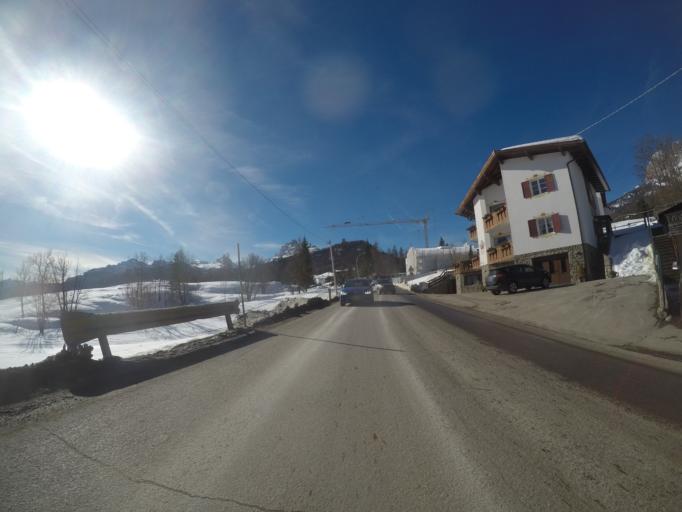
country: IT
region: Veneto
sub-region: Provincia di Belluno
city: Cortina d'Ampezzo
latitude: 46.5372
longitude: 12.1249
